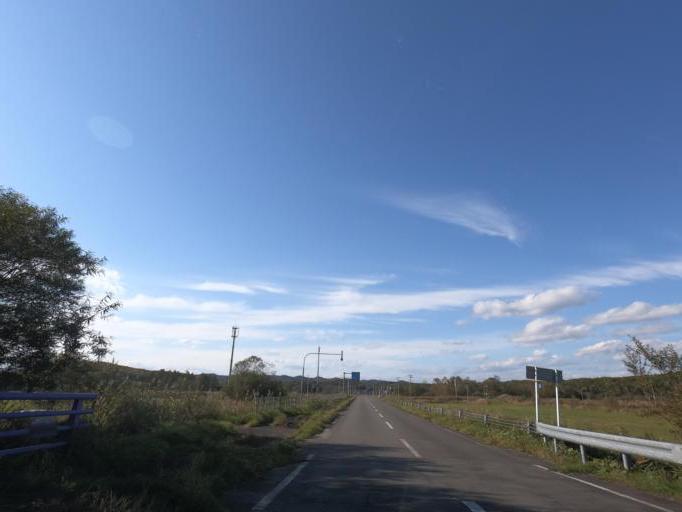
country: JP
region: Hokkaido
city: Obihiro
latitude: 42.6405
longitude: 143.5082
